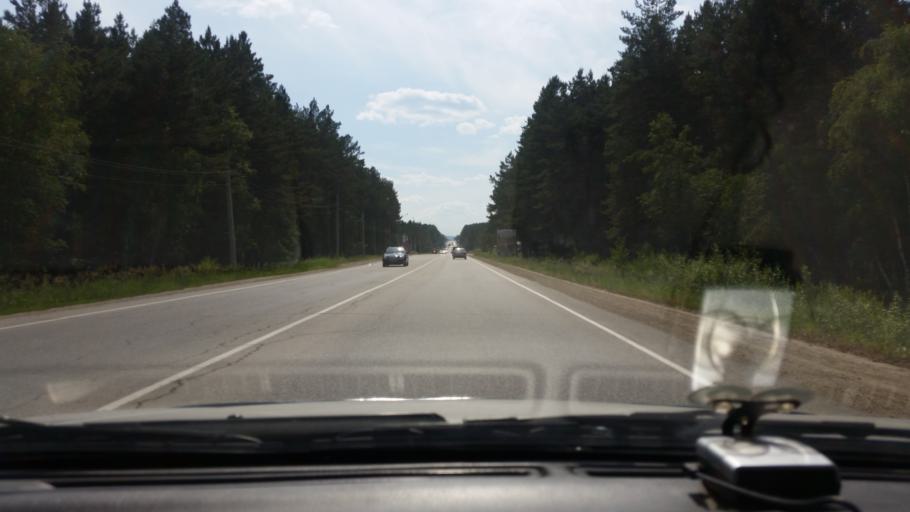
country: RU
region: Irkutsk
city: Shelekhov
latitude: 52.2173
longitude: 104.1283
